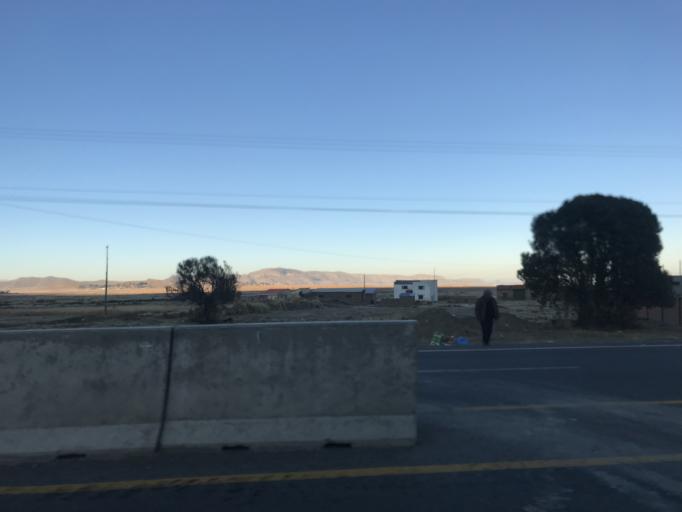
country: BO
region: La Paz
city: Batallas
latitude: -16.2525
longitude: -68.5678
